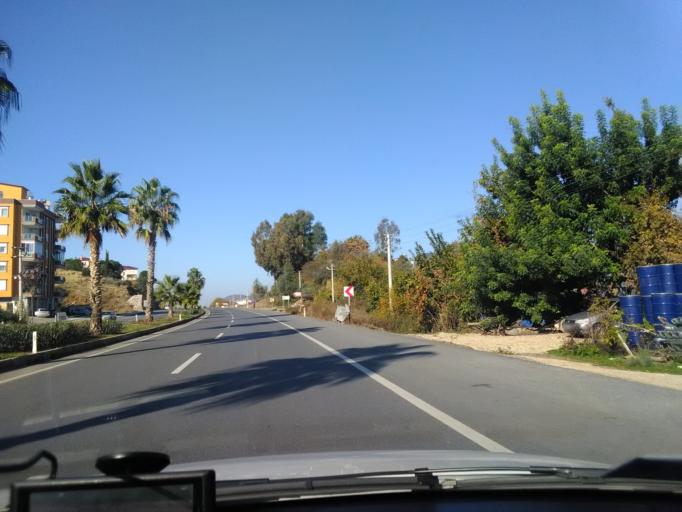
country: TR
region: Antalya
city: Gazipasa
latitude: 36.2547
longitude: 32.3338
